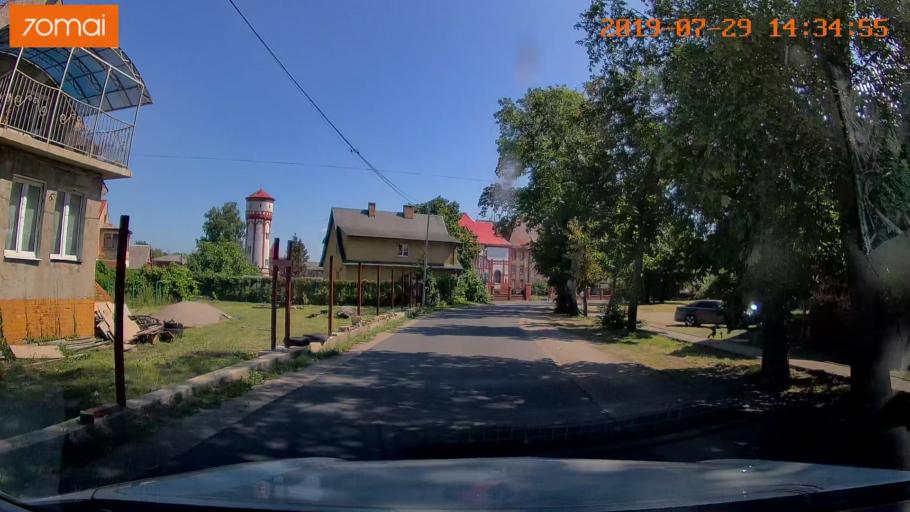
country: RU
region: Kaliningrad
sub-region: Gorod Kaliningrad
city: Baltiysk
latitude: 54.6453
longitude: 19.8911
